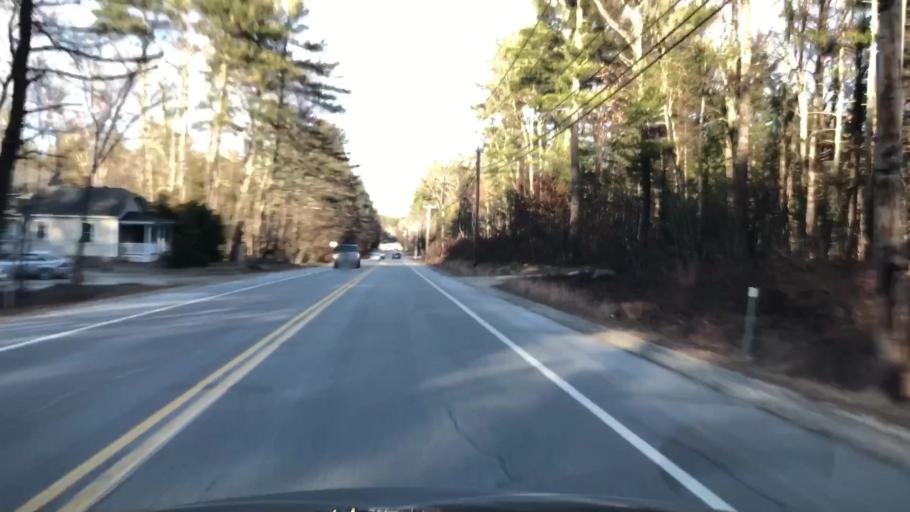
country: US
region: New Hampshire
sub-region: Hillsborough County
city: Milford
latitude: 42.7953
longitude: -71.6555
